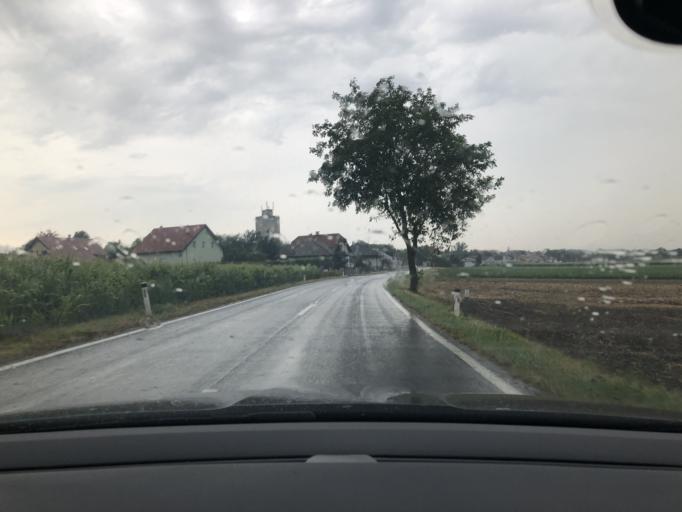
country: AT
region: Lower Austria
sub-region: Politischer Bezirk Ganserndorf
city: Angern an der March
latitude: 48.3056
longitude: 16.8393
